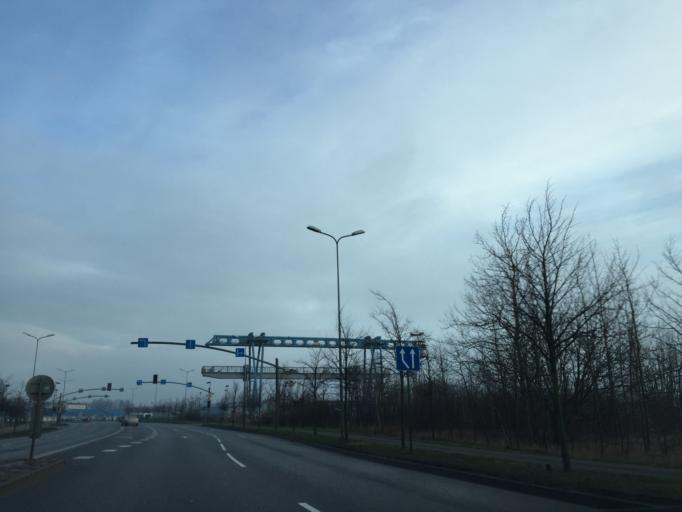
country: LV
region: Liepaja
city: Liepaja
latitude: 56.5189
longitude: 21.0264
